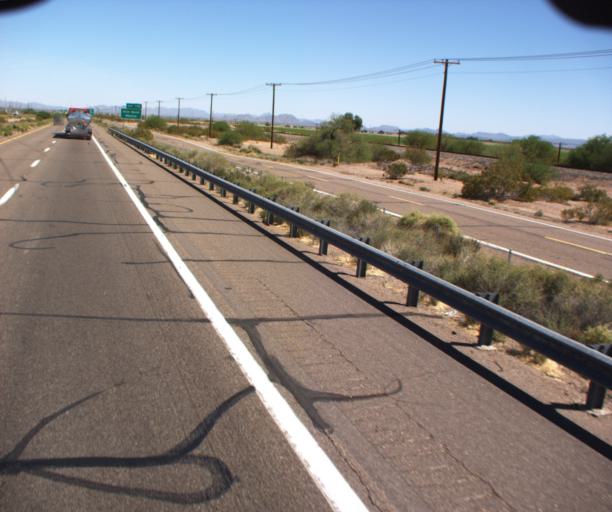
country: US
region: Arizona
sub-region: Maricopa County
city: Gila Bend
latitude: 32.9372
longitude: -112.7697
